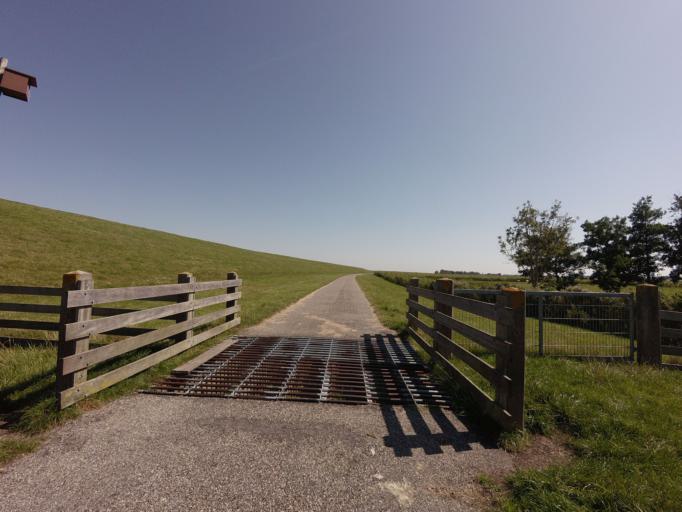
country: NL
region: Friesland
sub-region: Gemeente Dongeradeel
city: Anjum
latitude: 53.4016
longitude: 6.0912
